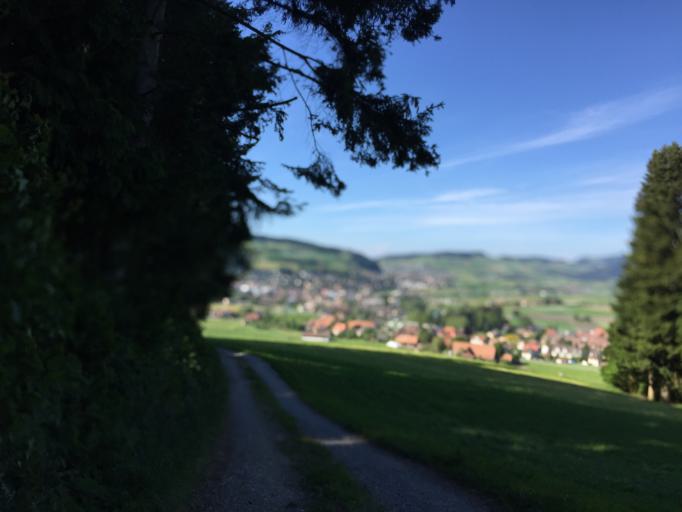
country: CH
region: Bern
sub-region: Bern-Mittelland District
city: Konolfingen
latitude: 46.8647
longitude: 7.6177
